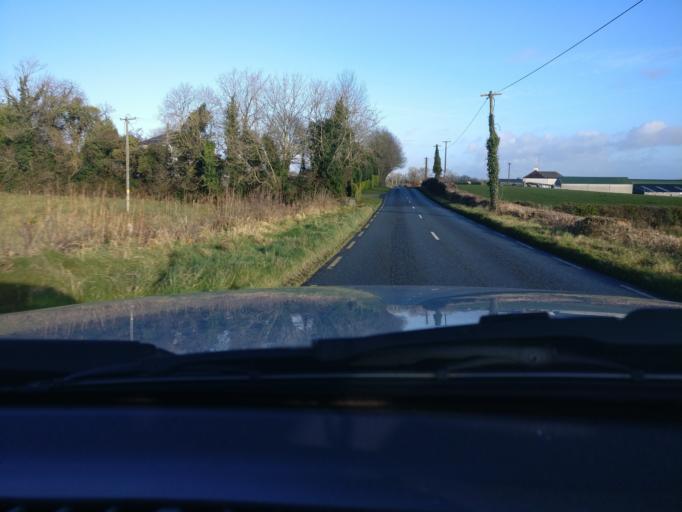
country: IE
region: Leinster
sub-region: An Iarmhi
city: An Muileann gCearr
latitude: 53.4903
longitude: -7.4394
